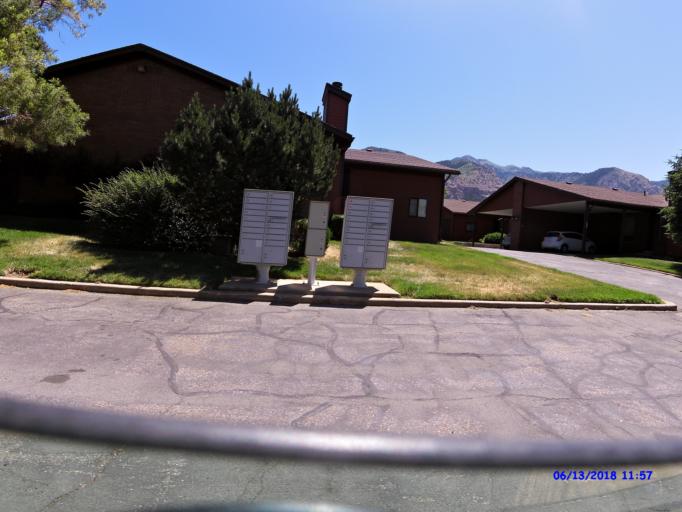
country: US
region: Utah
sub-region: Weber County
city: Ogden
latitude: 41.2310
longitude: -111.9450
